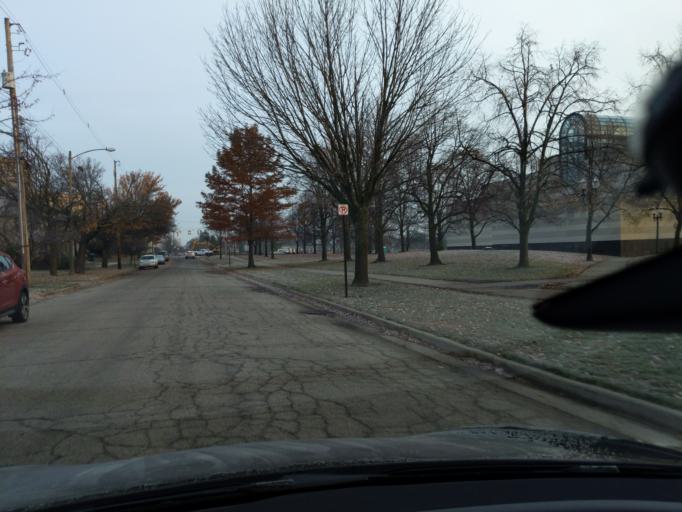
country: US
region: Michigan
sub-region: Ingham County
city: Lansing
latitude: 42.7315
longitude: -84.5646
